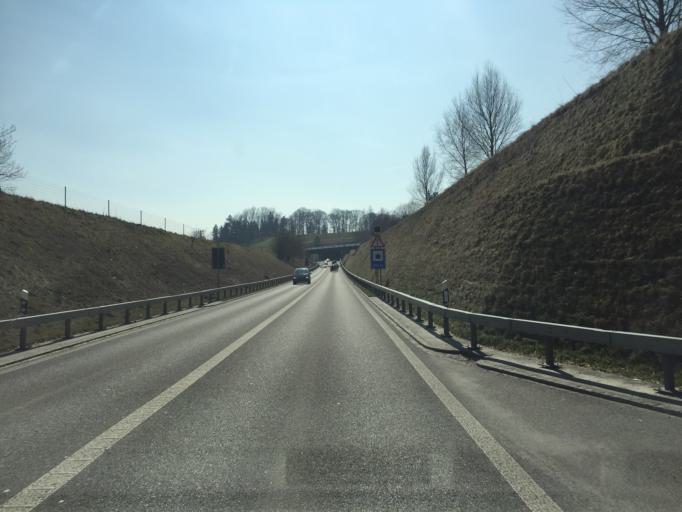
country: CH
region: Saint Gallen
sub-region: Wahlkreis Wil
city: Jonschwil
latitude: 47.4136
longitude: 9.0723
